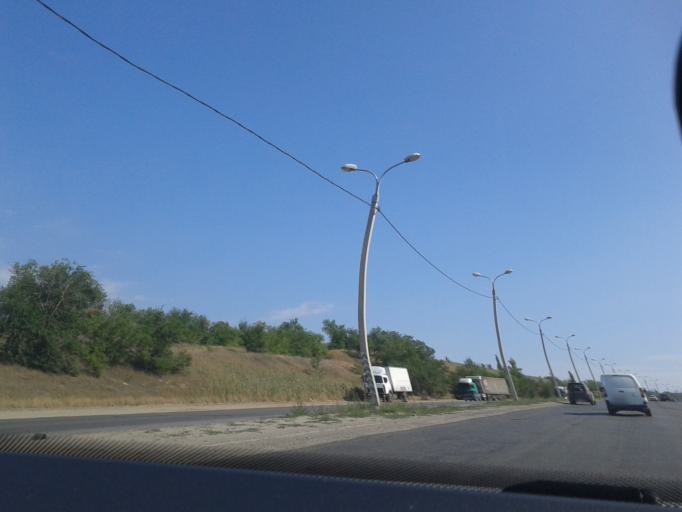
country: RU
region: Volgograd
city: Volgograd
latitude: 48.7243
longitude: 44.4468
